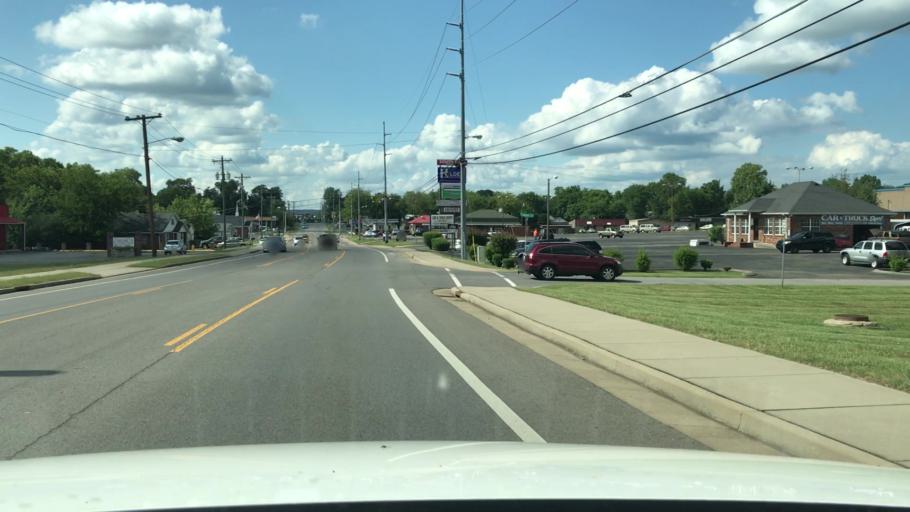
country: US
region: Tennessee
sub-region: Sumner County
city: Gallatin
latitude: 36.3775
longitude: -86.4422
